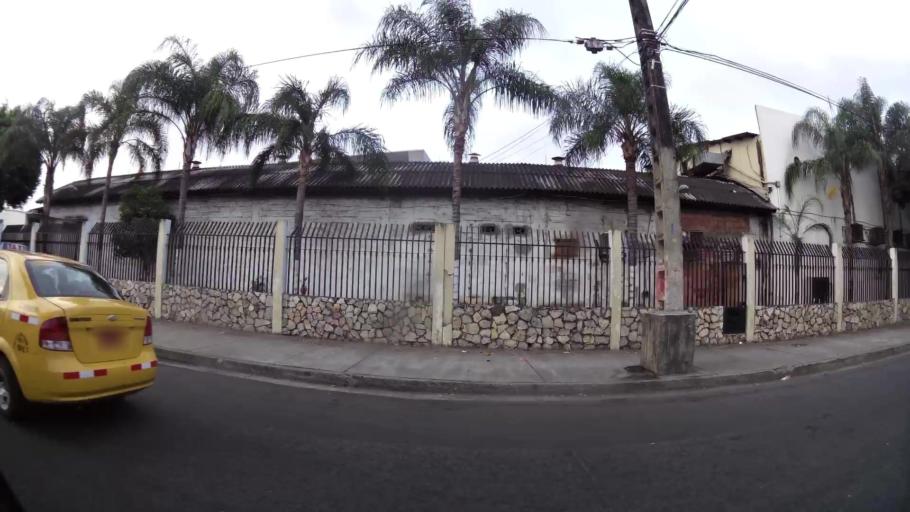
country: EC
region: Guayas
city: Eloy Alfaro
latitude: -2.1765
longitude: -79.8864
